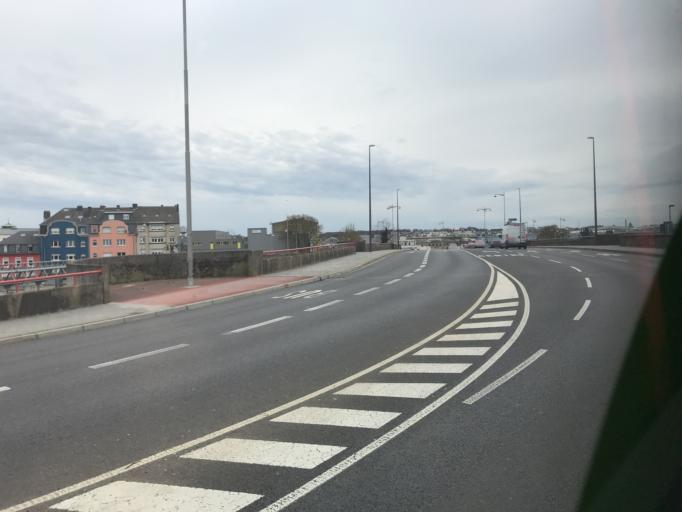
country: LU
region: Luxembourg
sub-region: Canton de Luxembourg
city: Luxembourg
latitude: 49.5962
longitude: 6.1314
